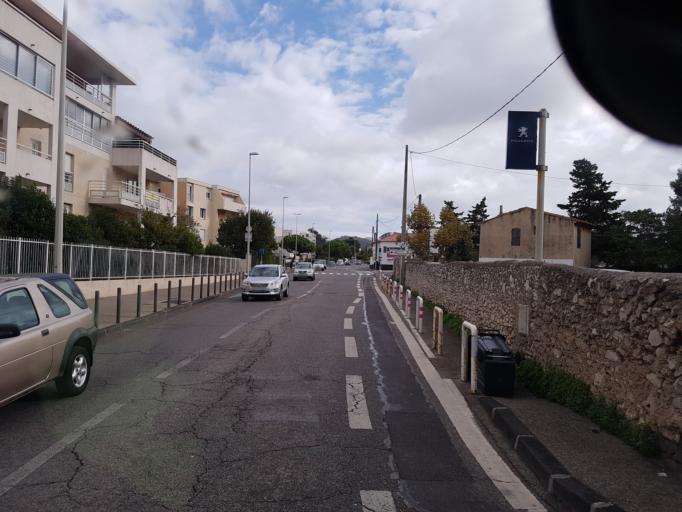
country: FR
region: Provence-Alpes-Cote d'Azur
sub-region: Departement des Bouches-du-Rhone
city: Marseille 09
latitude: 43.2465
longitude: 5.3876
